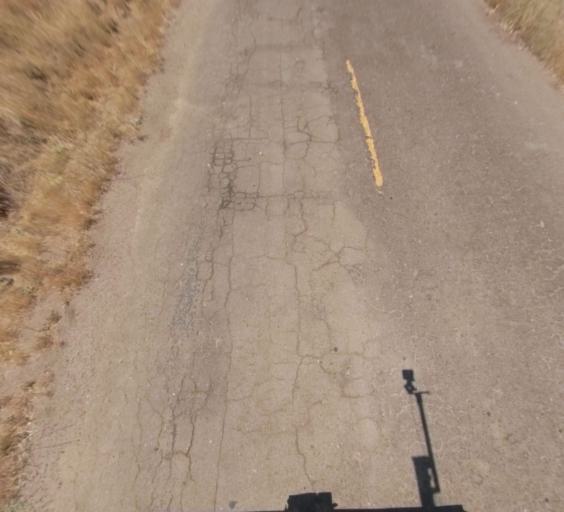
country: US
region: California
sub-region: Madera County
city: Madera Acres
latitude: 37.0875
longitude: -120.0127
